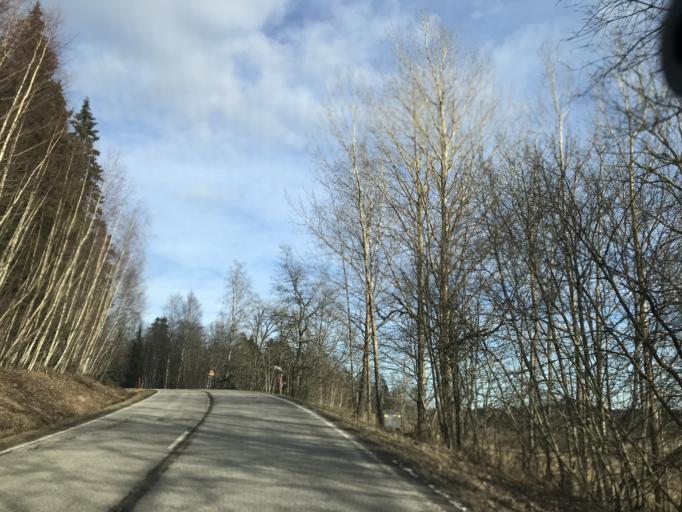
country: FI
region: Uusimaa
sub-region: Raaseporin
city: Pohja
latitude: 60.0888
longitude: 23.4220
